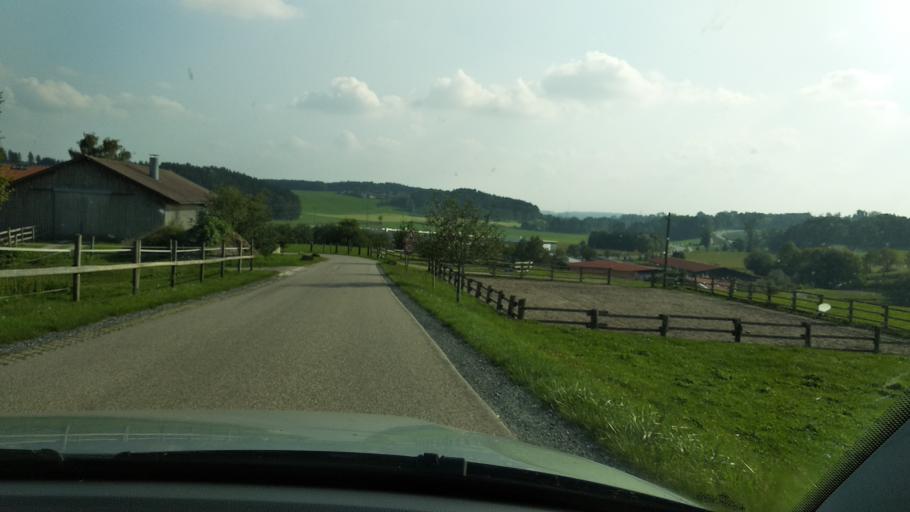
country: DE
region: Bavaria
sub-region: Upper Bavaria
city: Ebersberg
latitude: 48.0835
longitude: 11.9863
